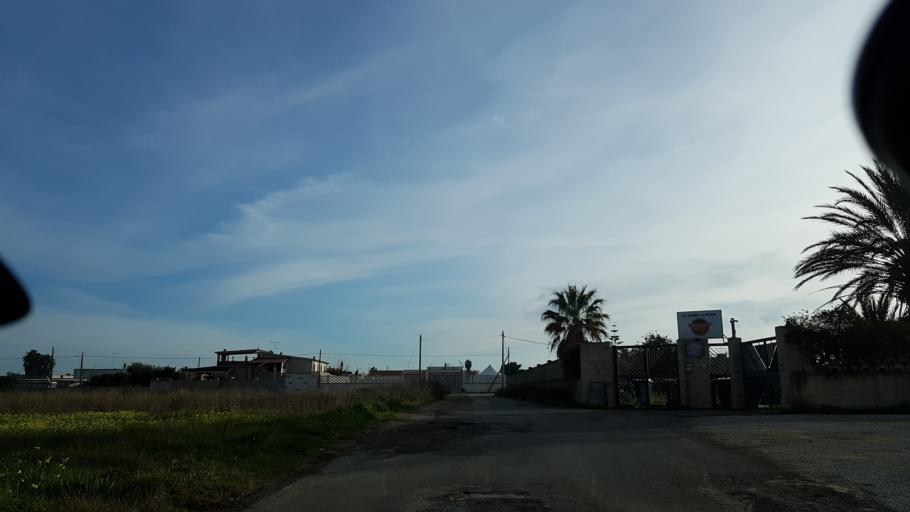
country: IT
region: Apulia
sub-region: Provincia di Brindisi
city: Brindisi
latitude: 40.6162
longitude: 17.9239
